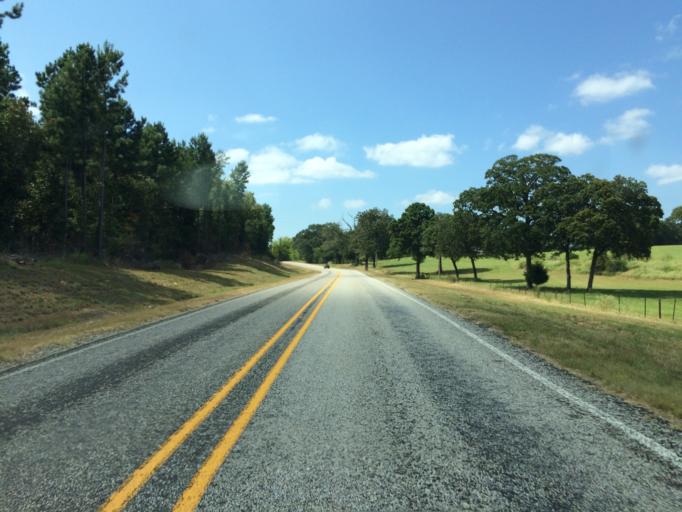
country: US
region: Texas
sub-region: Wood County
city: Hawkins
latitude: 32.6473
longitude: -95.2352
